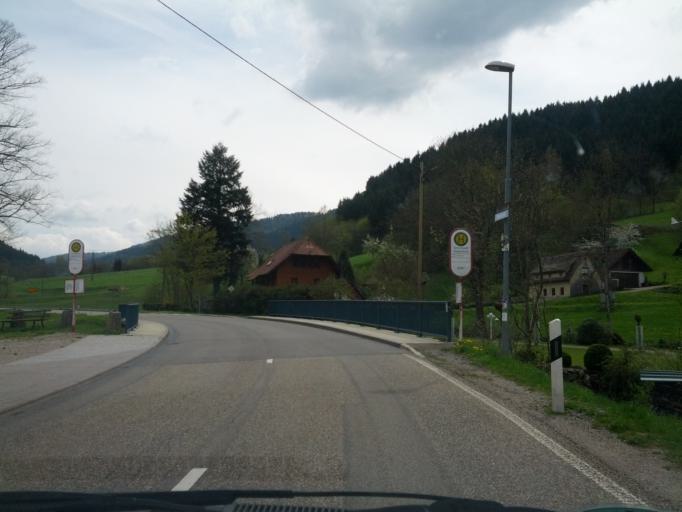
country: DE
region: Baden-Wuerttemberg
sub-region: Freiburg Region
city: Gutenbach
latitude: 48.0749
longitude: 8.0957
